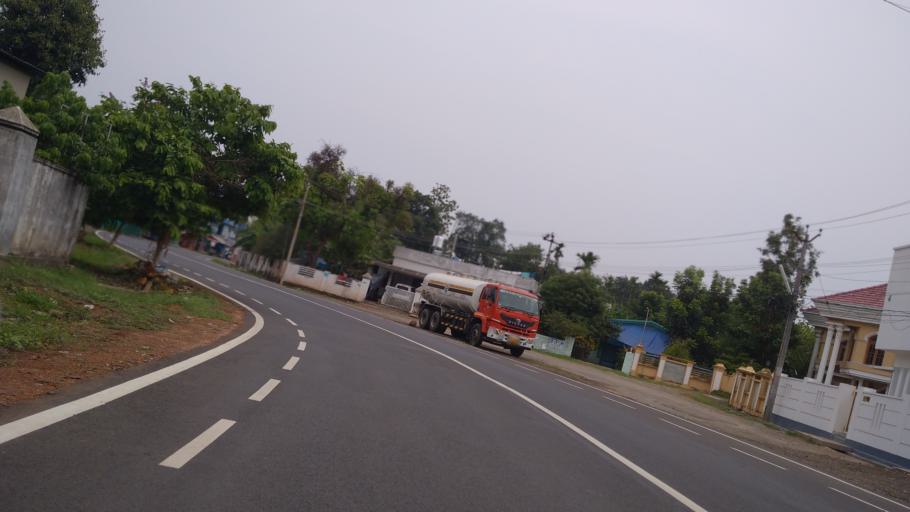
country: IN
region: Kerala
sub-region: Ernakulam
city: Angamali
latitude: 10.1802
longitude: 76.3976
